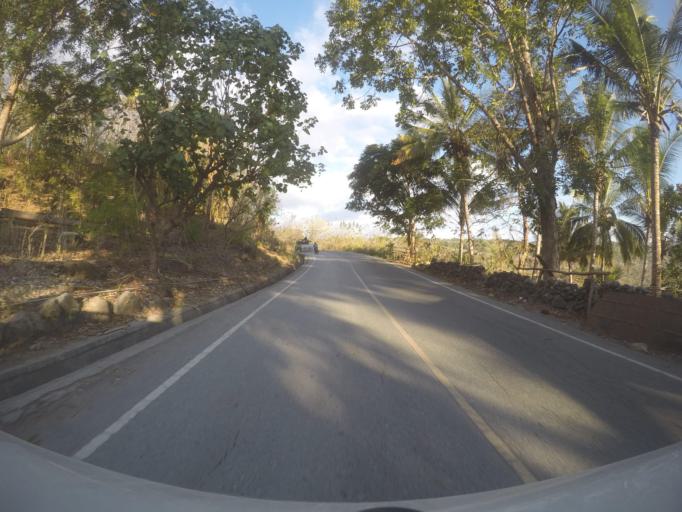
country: TL
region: Bobonaro
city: Maliana
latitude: -8.9622
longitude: 125.0334
